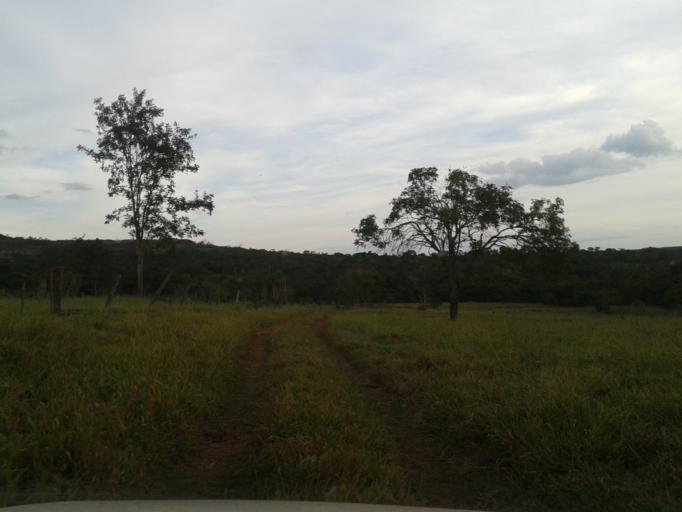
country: BR
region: Minas Gerais
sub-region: Campina Verde
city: Campina Verde
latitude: -19.4145
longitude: -49.6043
